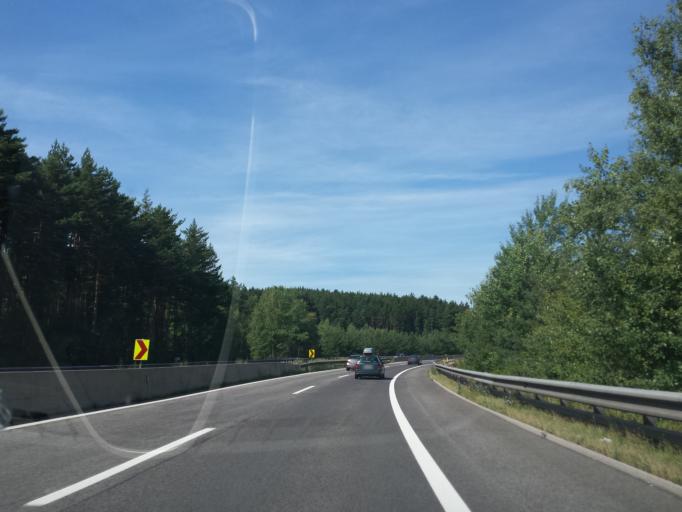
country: AT
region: Lower Austria
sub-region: Politischer Bezirk Neunkirchen
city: Buchbach
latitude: 47.6699
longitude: 15.9818
